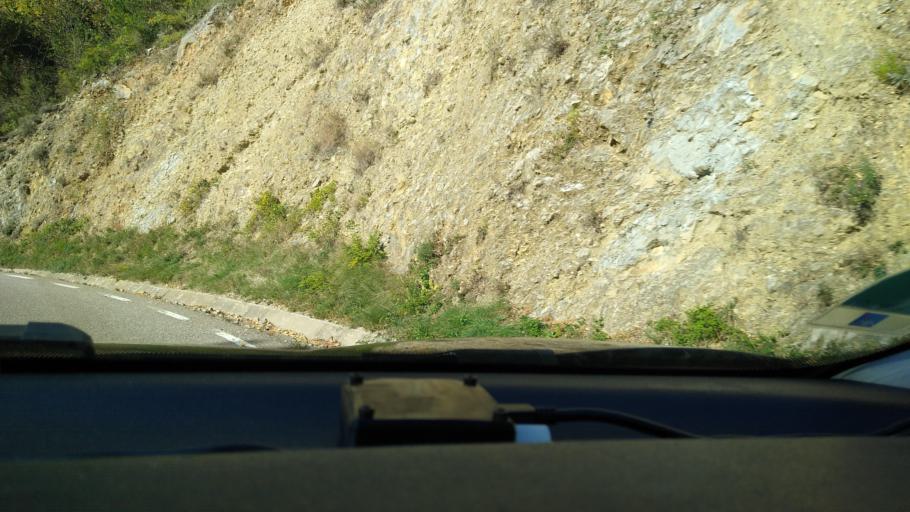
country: ES
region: Catalonia
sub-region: Provincia de Barcelona
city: Vallcebre
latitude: 42.1824
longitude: 1.8616
